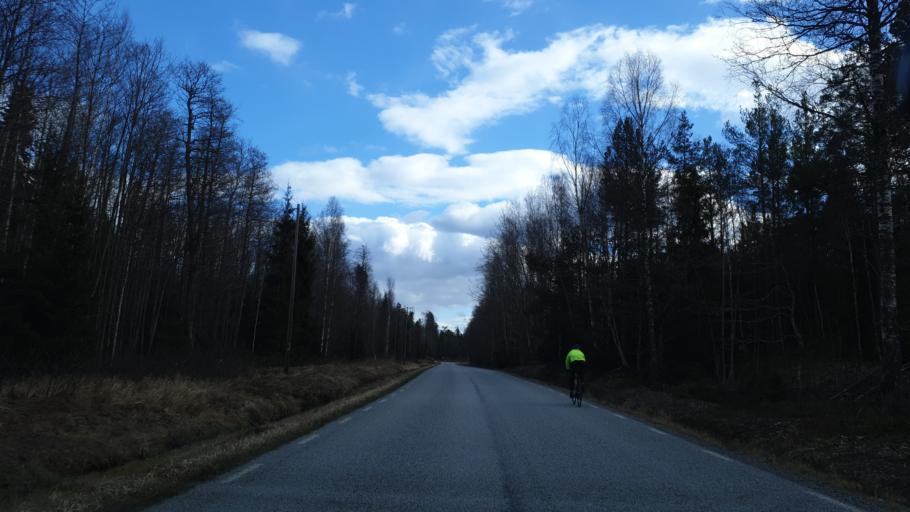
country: SE
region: Stockholm
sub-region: Varmdo Kommun
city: Hemmesta
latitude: 59.2346
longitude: 18.4806
